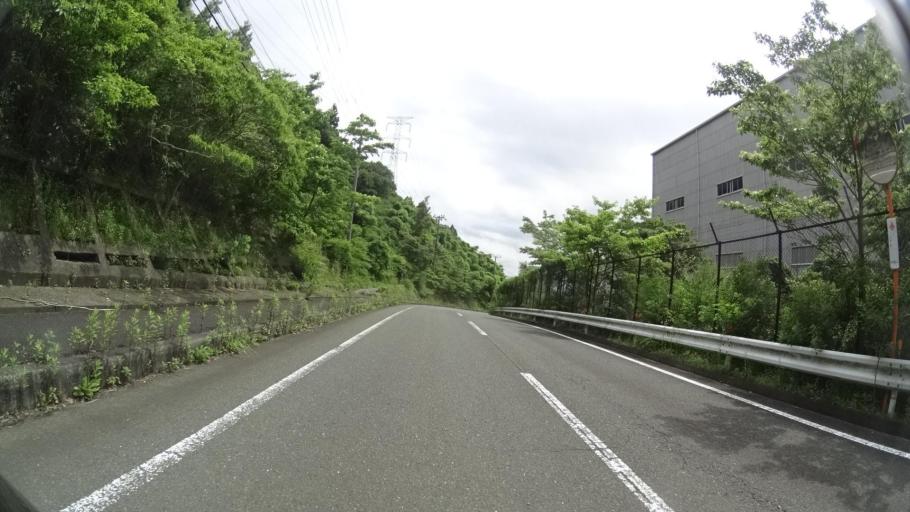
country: JP
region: Kyoto
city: Maizuru
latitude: 35.5299
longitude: 135.3462
